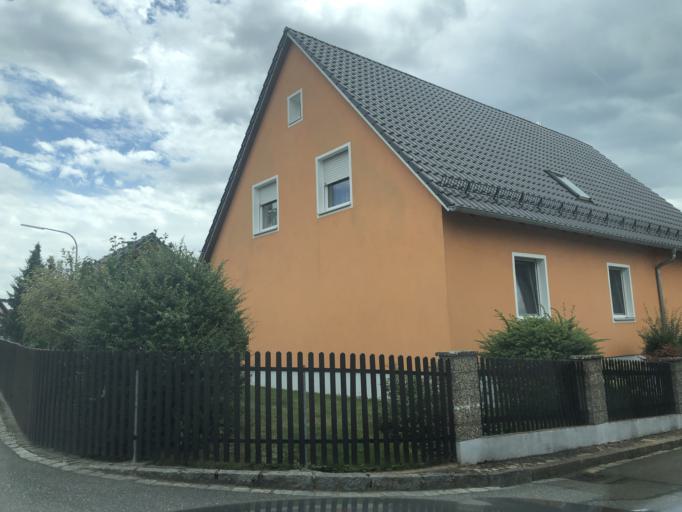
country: DE
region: Bavaria
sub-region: Upper Palatinate
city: Pressath
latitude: 49.7641
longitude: 11.9470
